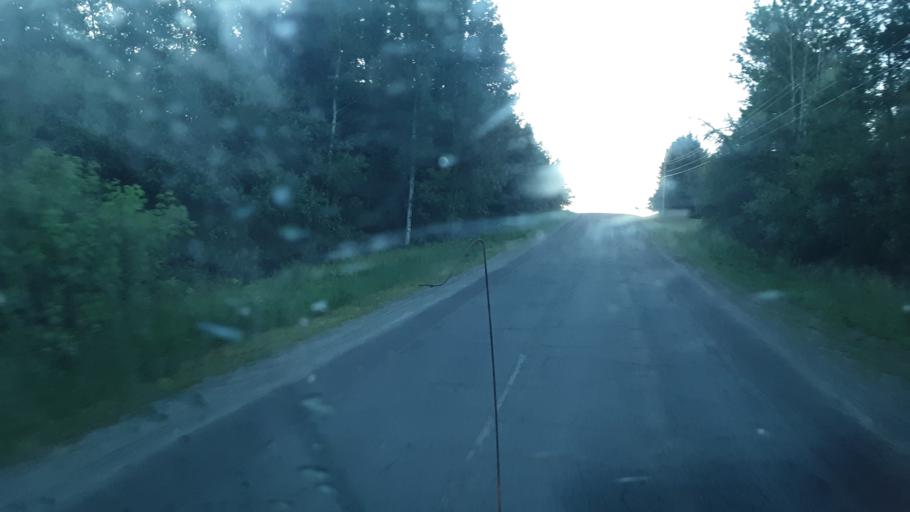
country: US
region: Maine
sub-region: Aroostook County
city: Caribou
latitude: 46.8027
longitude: -68.1159
